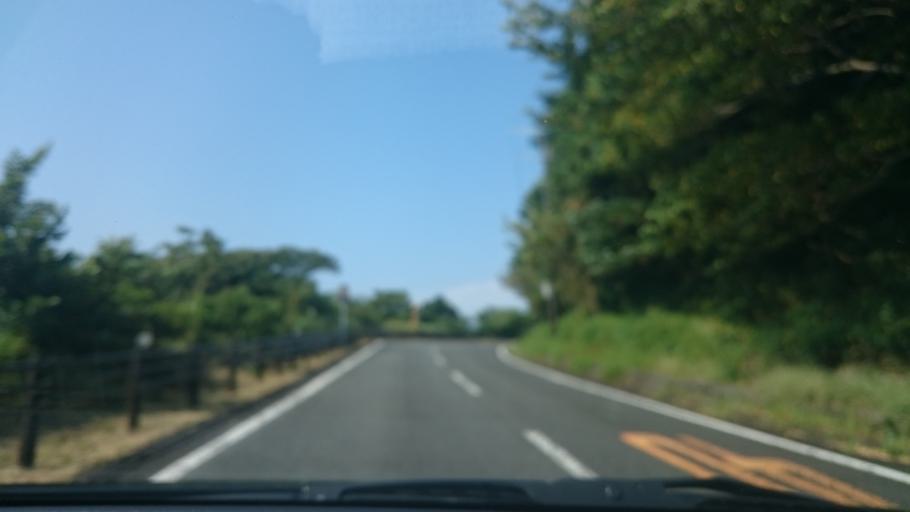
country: JP
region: Shizuoka
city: Heda
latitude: 34.9838
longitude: 138.7705
